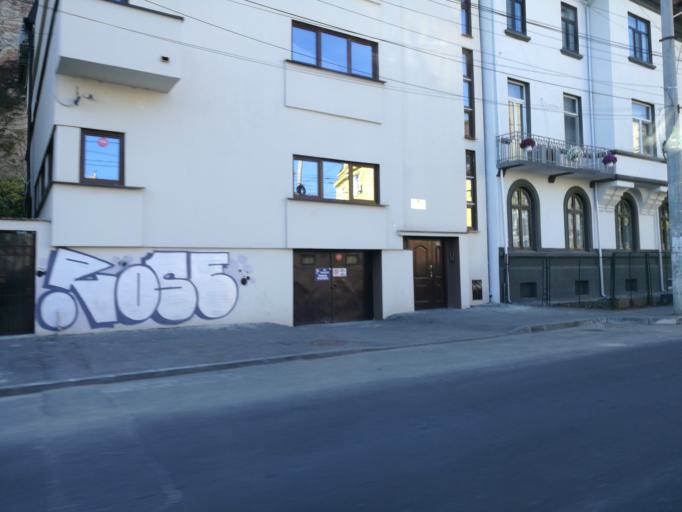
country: RO
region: Bucuresti
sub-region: Municipiul Bucuresti
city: Bucharest
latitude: 44.4410
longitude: 26.1206
